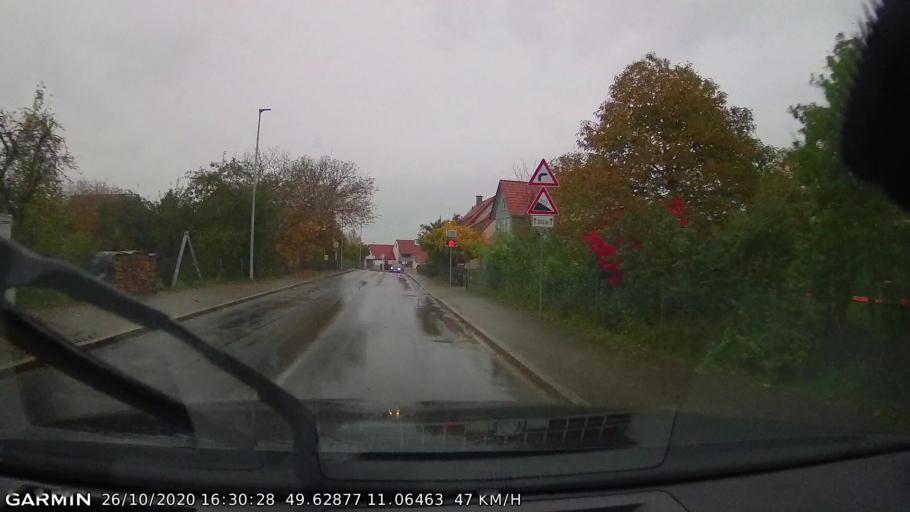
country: DE
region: Bavaria
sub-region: Regierungsbezirk Mittelfranken
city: Marloffstein
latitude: 49.6287
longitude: 11.0647
